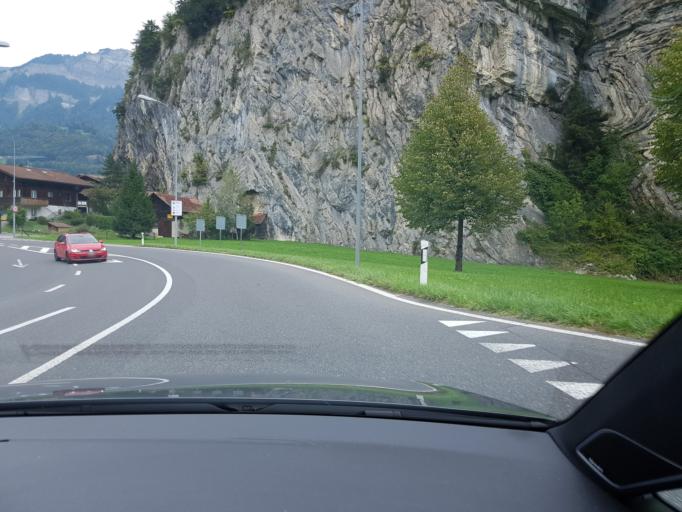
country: CH
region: Bern
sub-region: Interlaken-Oberhasli District
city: Brienz
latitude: 46.7447
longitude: 8.0602
